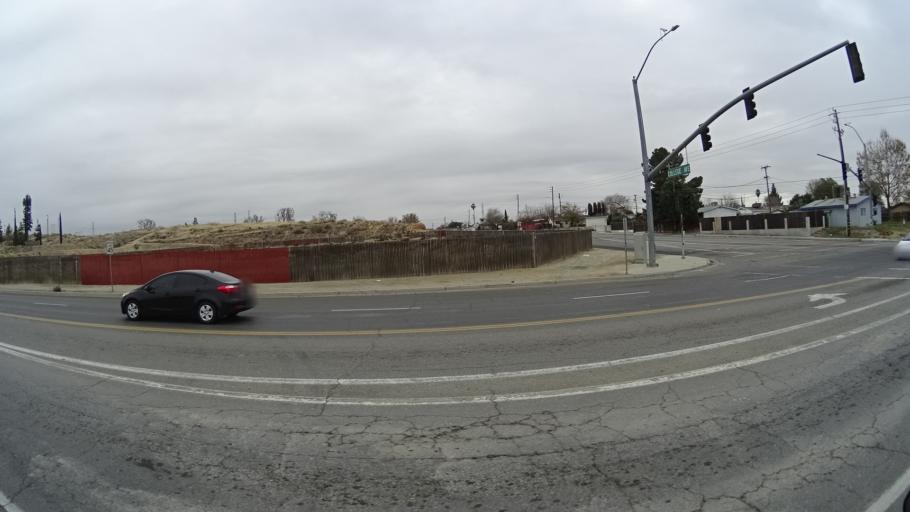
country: US
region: California
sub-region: Kern County
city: Bakersfield
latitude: 35.3836
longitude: -118.9303
